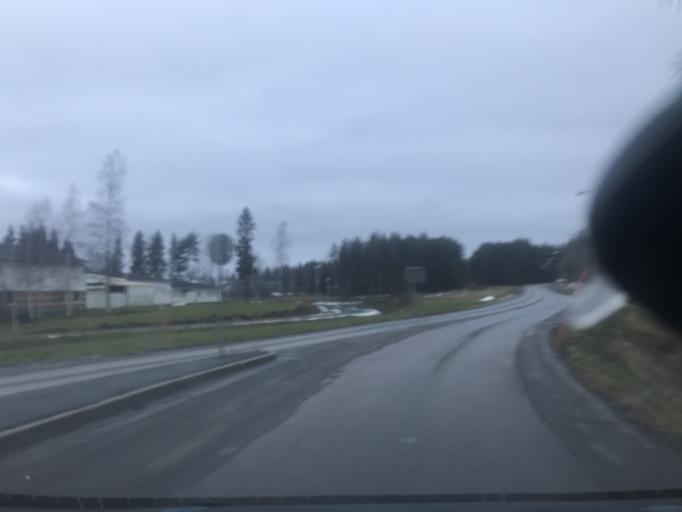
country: SE
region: Norrbotten
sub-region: Lulea Kommun
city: Bergnaset
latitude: 65.6154
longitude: 22.1231
